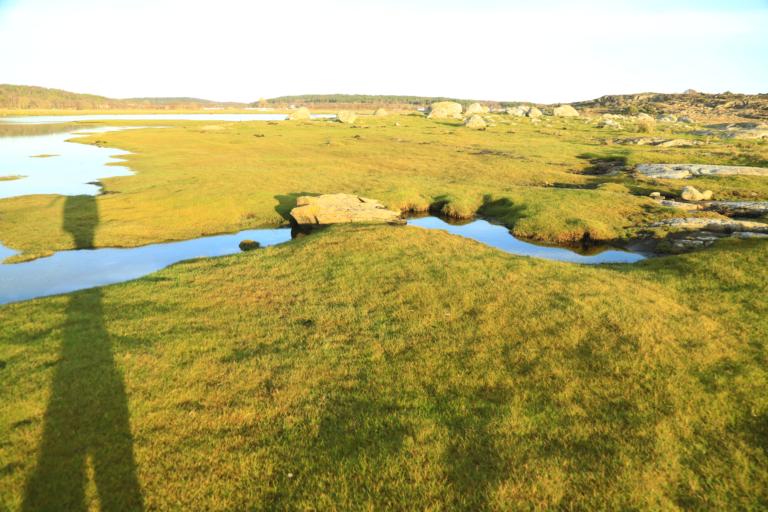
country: SE
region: Halland
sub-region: Varbergs Kommun
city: Varberg
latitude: 57.1617
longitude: 12.2217
